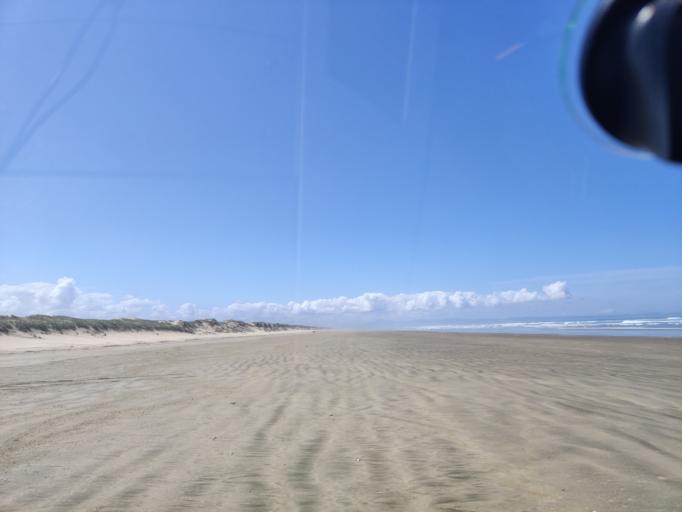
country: NZ
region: Northland
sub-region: Far North District
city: Kaitaia
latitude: -34.9357
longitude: 173.1121
